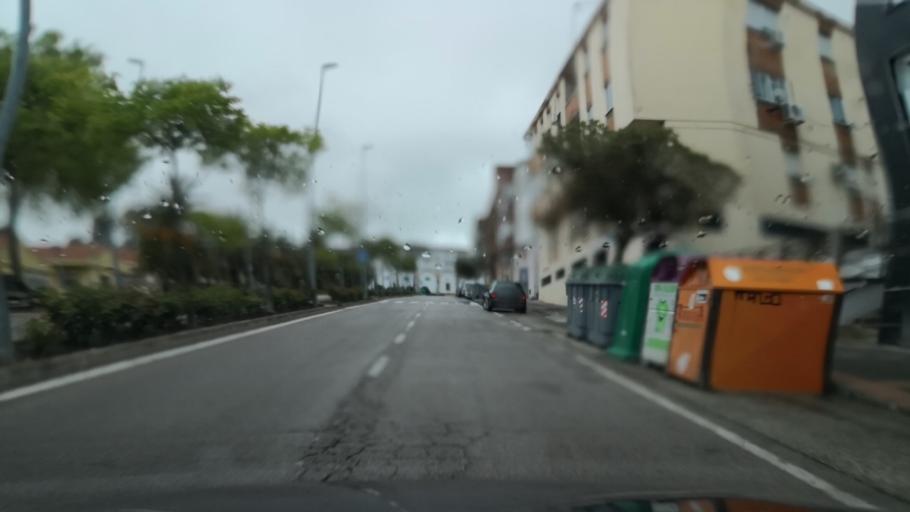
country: ES
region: Extremadura
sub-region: Provincia de Caceres
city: Caceres
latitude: 39.4800
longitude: -6.3782
